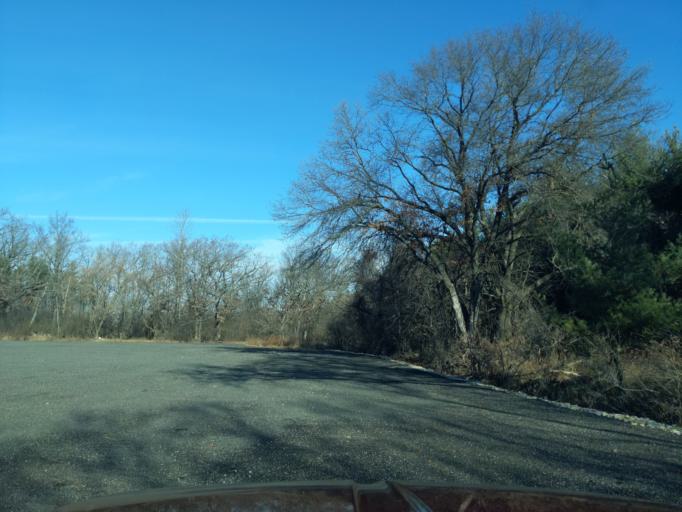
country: US
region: Wisconsin
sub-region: Waushara County
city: Silver Lake
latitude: 44.1222
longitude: -89.1791
